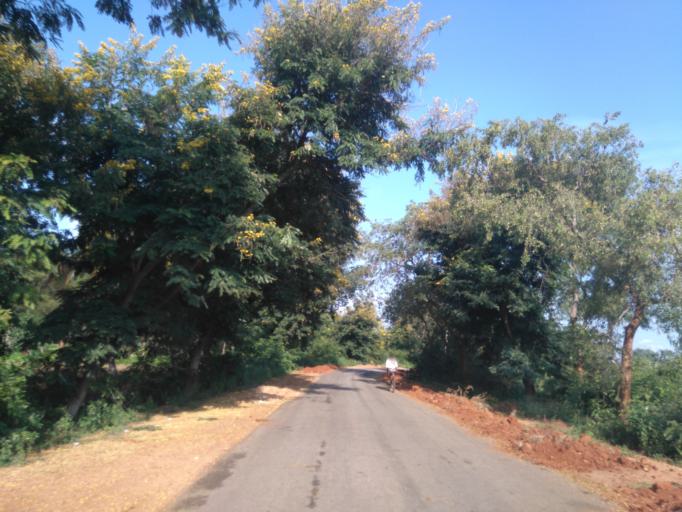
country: IN
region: Karnataka
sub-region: Mandya
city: Malavalli
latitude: 12.2640
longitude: 77.0314
